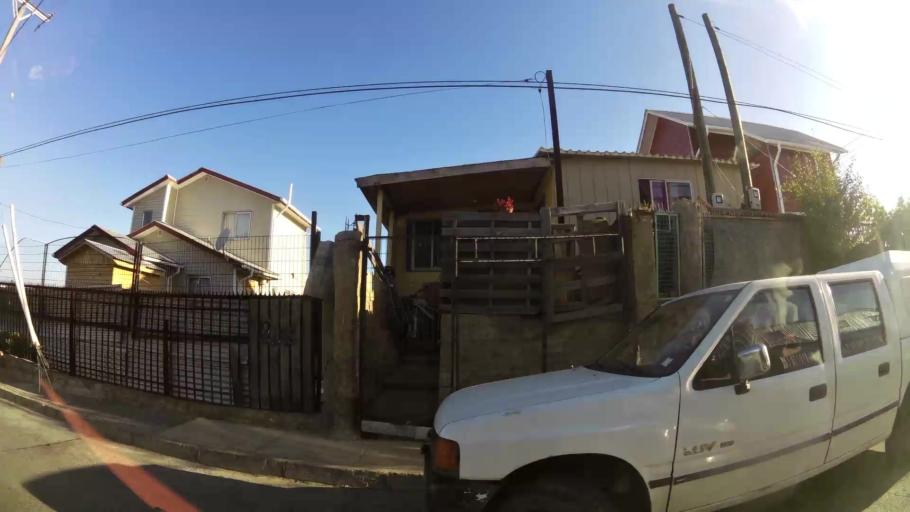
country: CL
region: Valparaiso
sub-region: Provincia de Valparaiso
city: Valparaiso
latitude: -33.0619
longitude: -71.6118
